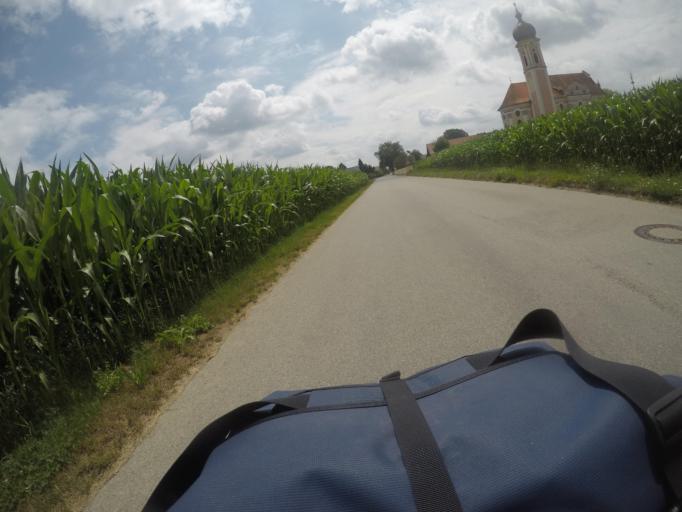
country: DE
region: Bavaria
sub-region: Swabia
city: Fellheim
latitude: 48.0941
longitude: 10.1544
